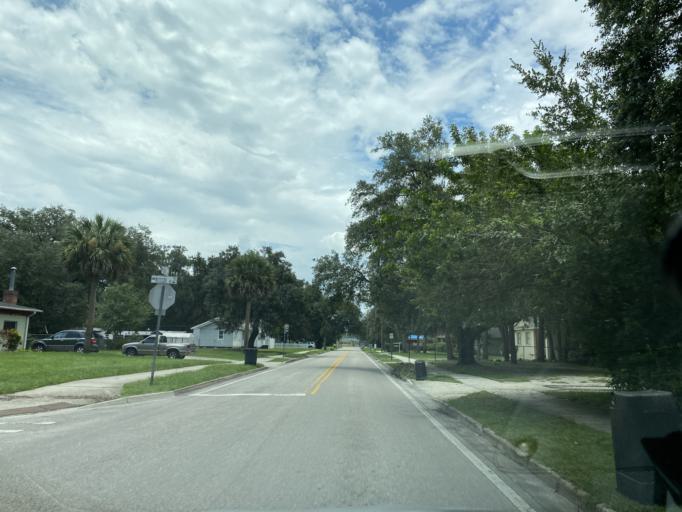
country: US
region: Florida
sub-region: Seminole County
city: Sanford
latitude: 28.7991
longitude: -81.2523
